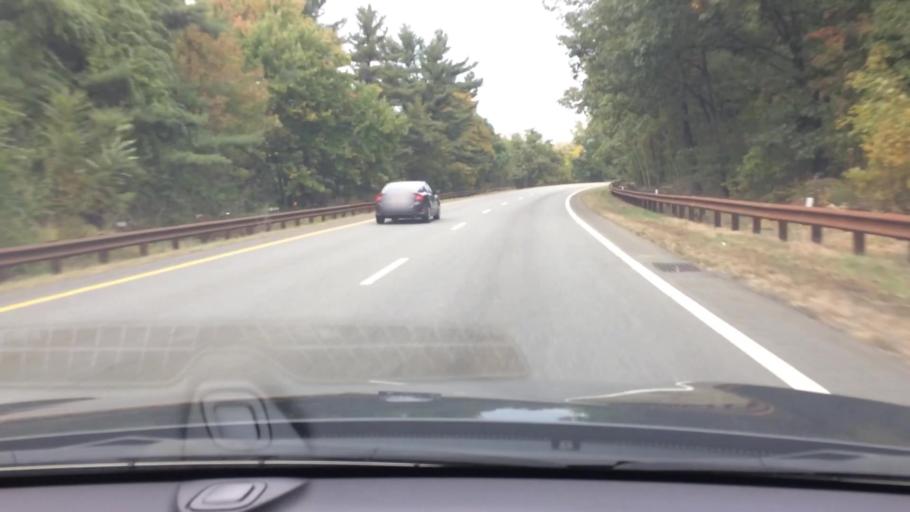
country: US
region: New Jersey
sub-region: Bergen County
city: Alpine
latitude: 40.9374
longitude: -73.9259
